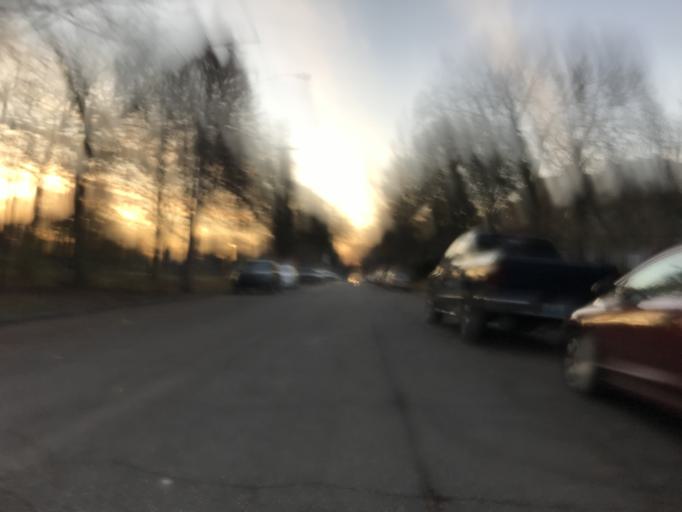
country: US
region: Kentucky
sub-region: Jefferson County
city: Louisville
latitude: 38.2315
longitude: -85.7616
